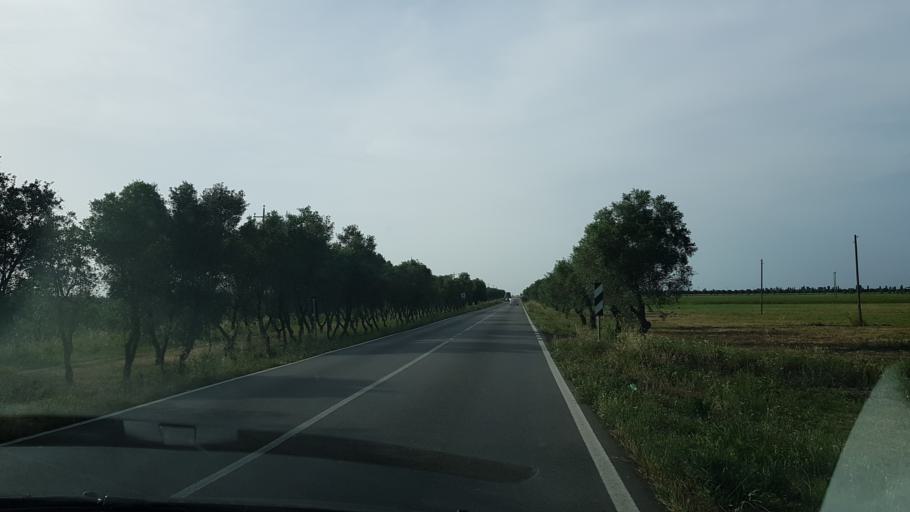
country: IT
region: Apulia
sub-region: Provincia di Brindisi
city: San Pancrazio Salentino
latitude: 40.3706
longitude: 17.8395
